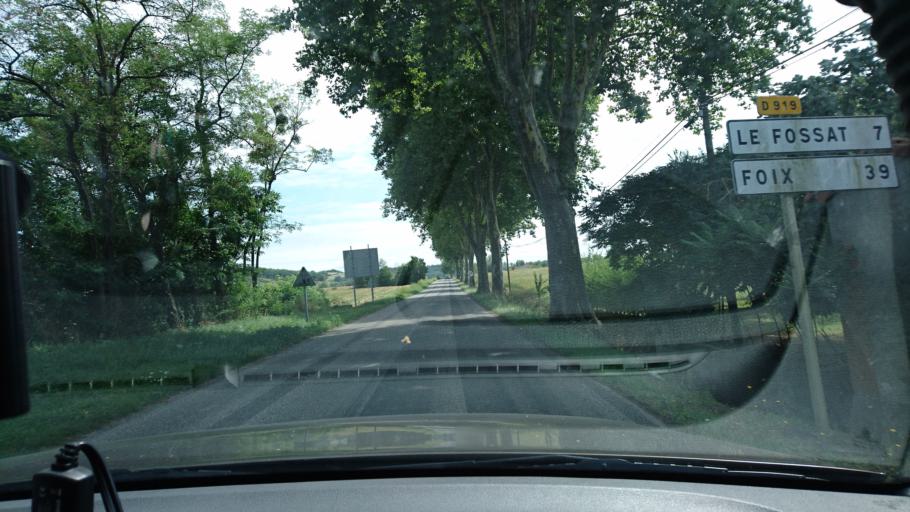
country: FR
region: Midi-Pyrenees
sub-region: Departement de l'Ariege
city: Lezat-sur-Leze
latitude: 43.2302
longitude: 1.3765
